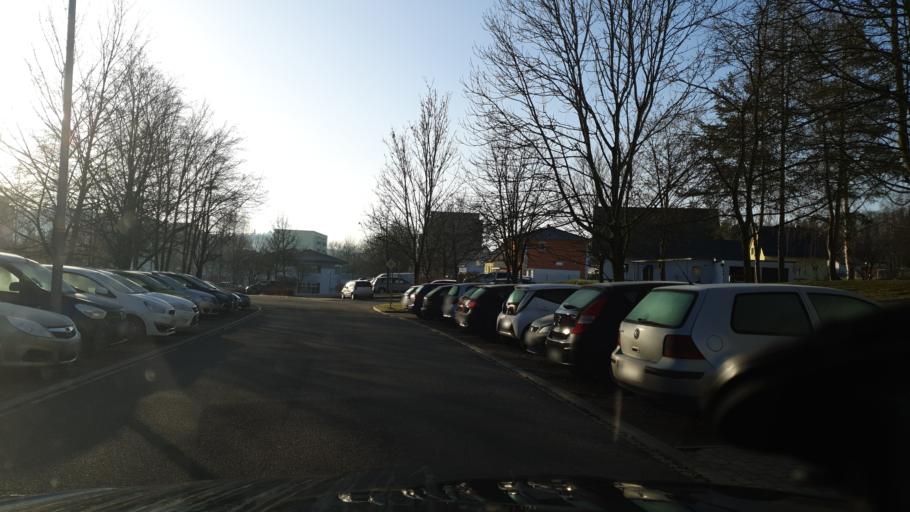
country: DE
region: Saxony
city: Floha
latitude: 50.8494
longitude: 13.0683
